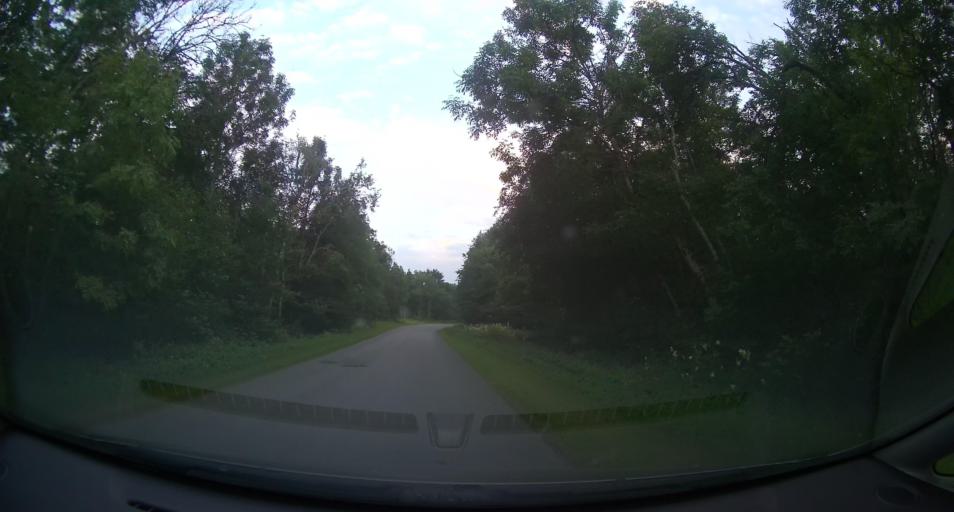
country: EE
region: Laeaene
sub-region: Lihula vald
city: Lihula
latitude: 58.5912
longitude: 23.6109
